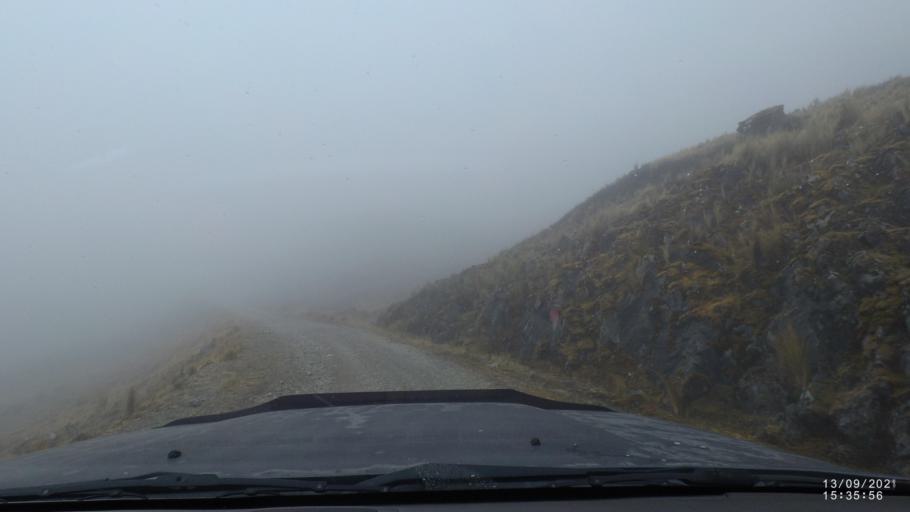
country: BO
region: Cochabamba
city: Colomi
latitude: -17.3319
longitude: -65.7322
